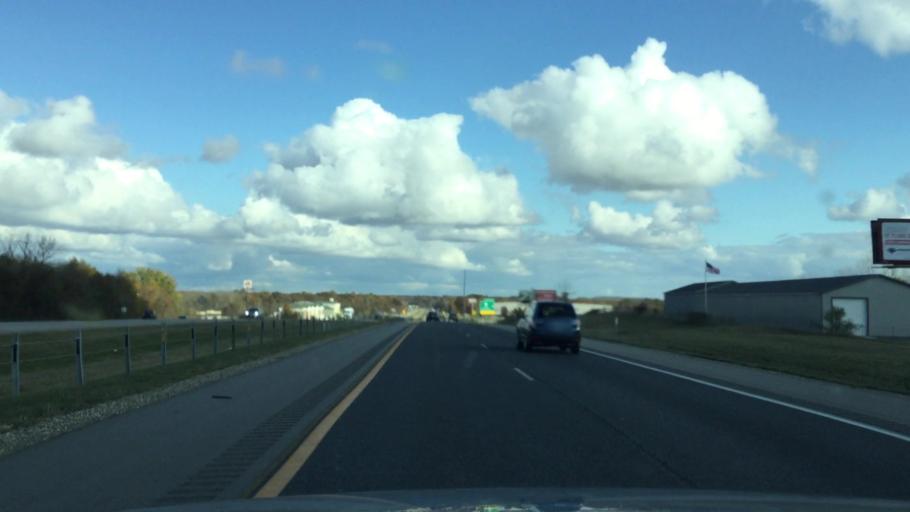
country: US
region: Michigan
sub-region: Berrien County
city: Watervliet
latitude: 42.1778
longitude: -86.2682
